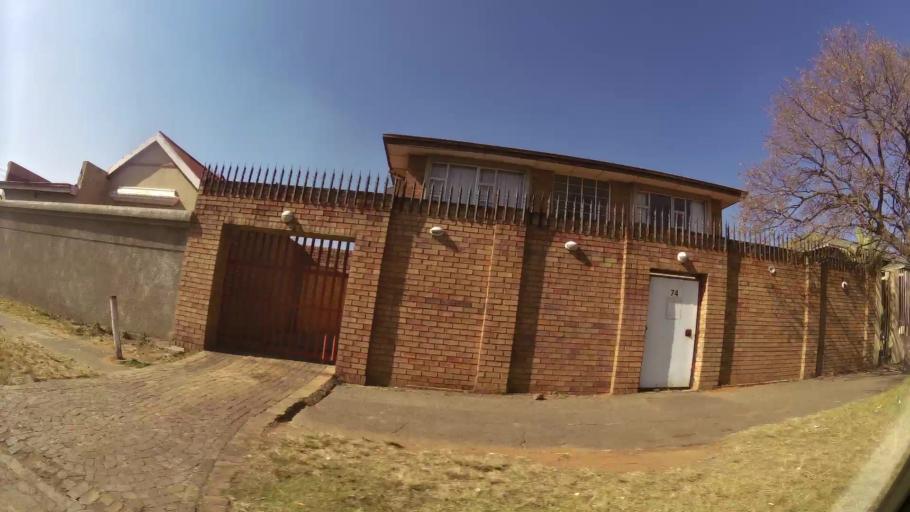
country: ZA
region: Gauteng
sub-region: City of Johannesburg Metropolitan Municipality
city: Johannesburg
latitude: -26.2522
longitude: 28.0390
